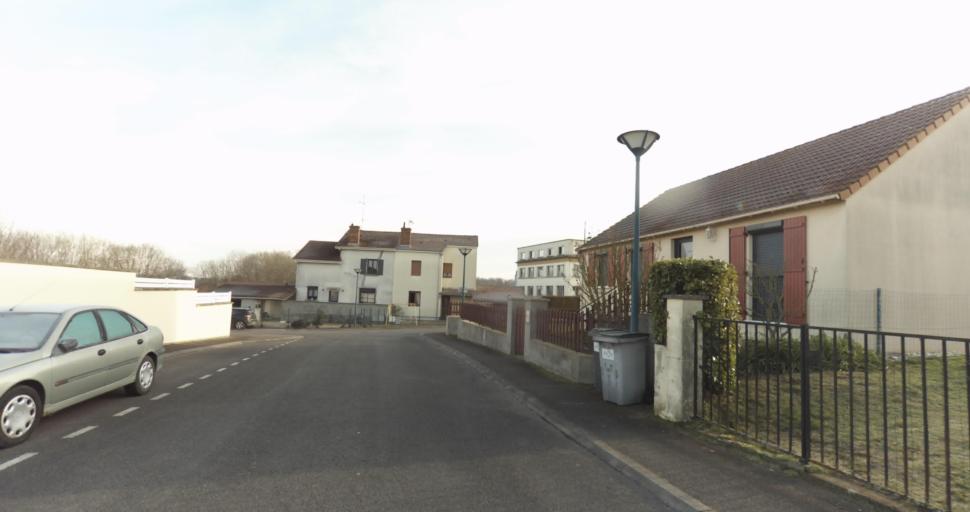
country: FR
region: Lorraine
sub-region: Departement de Meurthe-et-Moselle
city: Labry
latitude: 49.1671
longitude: 5.8886
